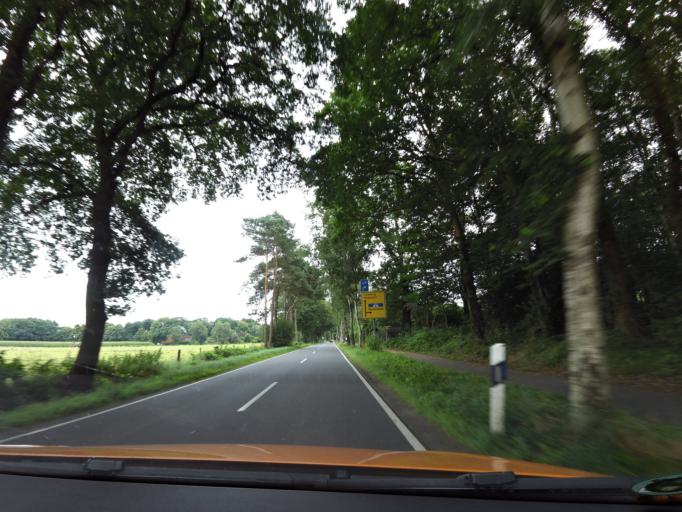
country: DE
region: Lower Saxony
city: Wiefelstede
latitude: 53.1974
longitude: 8.1299
